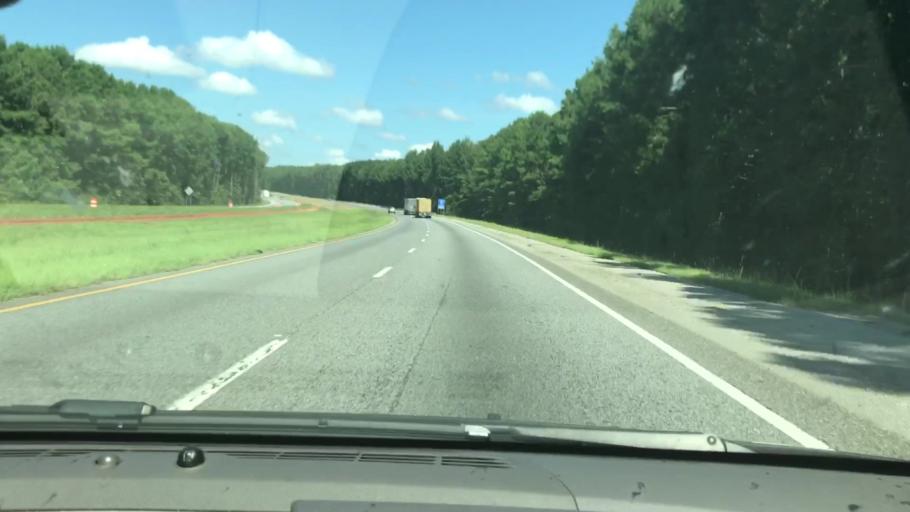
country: US
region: Georgia
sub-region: Harris County
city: Hamilton
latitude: 32.6927
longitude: -84.9938
